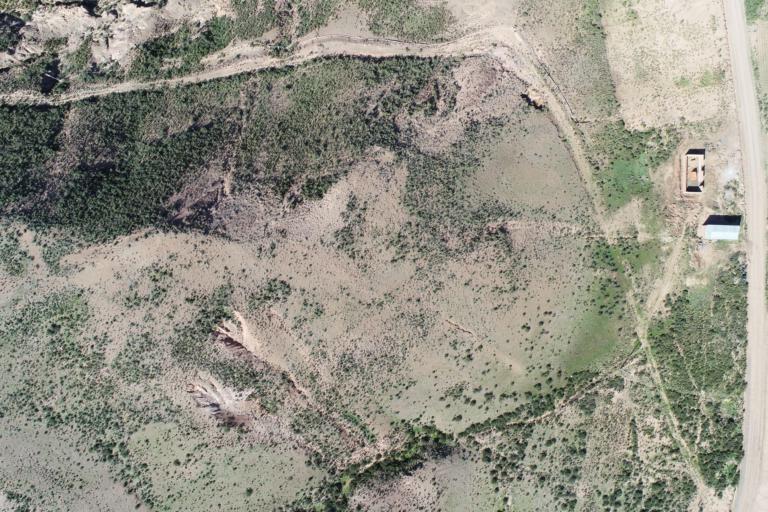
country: BO
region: La Paz
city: Curahuara de Carangas
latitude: -17.3024
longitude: -68.4862
